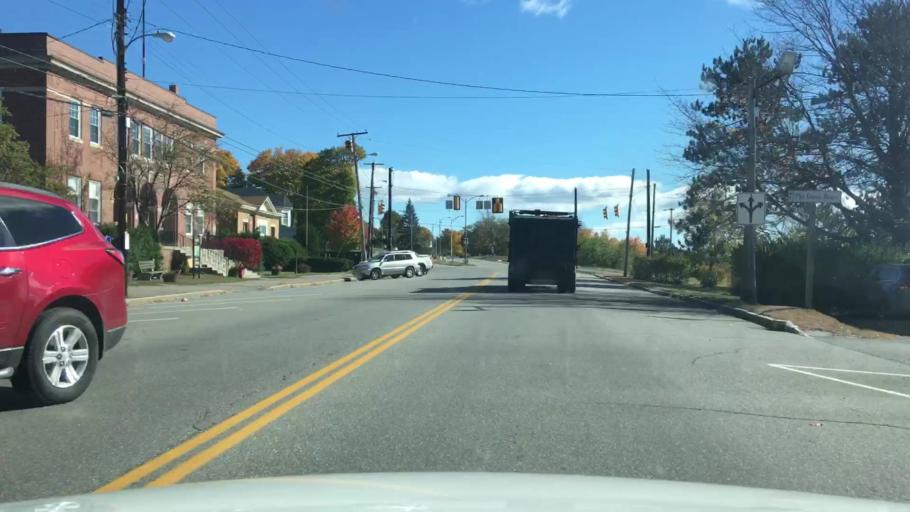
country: US
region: Maine
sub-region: Penobscot County
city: East Millinocket
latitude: 45.6255
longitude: -68.5758
